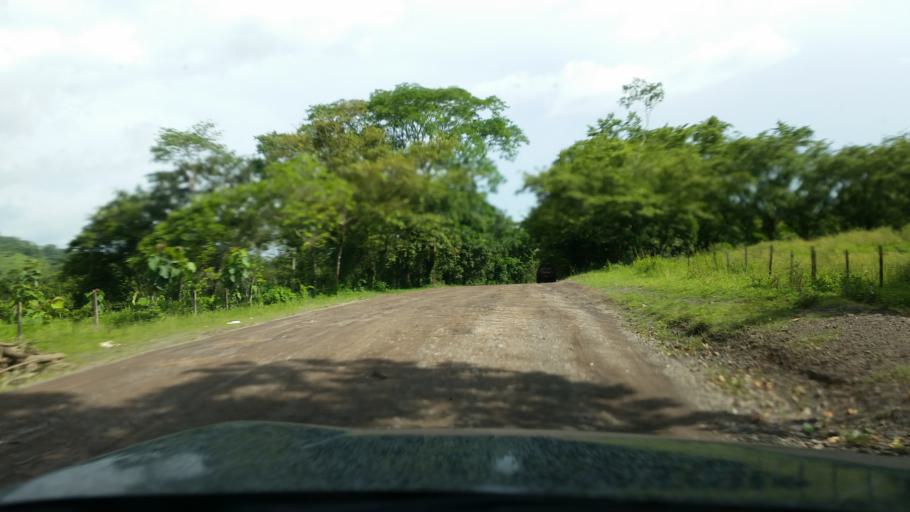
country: NI
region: Atlantico Norte (RAAN)
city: Siuna
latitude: 13.6770
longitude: -84.7902
